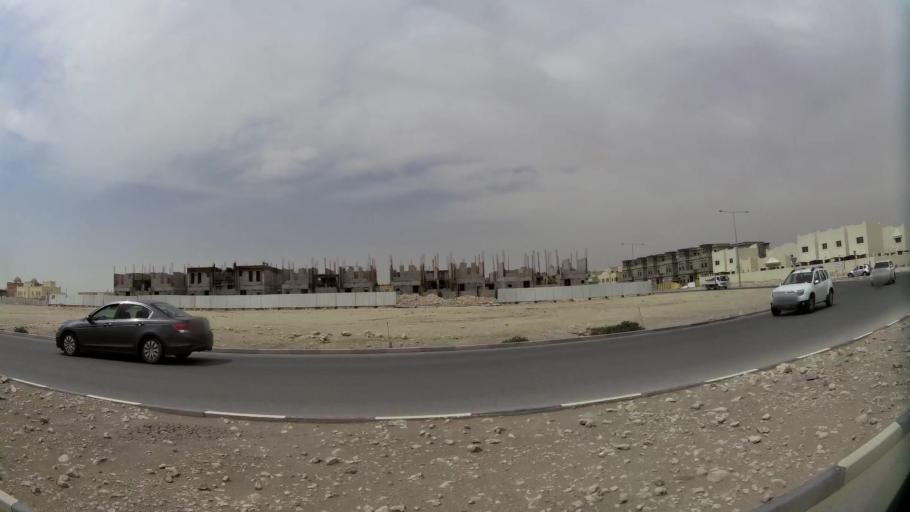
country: QA
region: Baladiyat ad Dawhah
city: Doha
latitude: 25.2184
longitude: 51.4780
